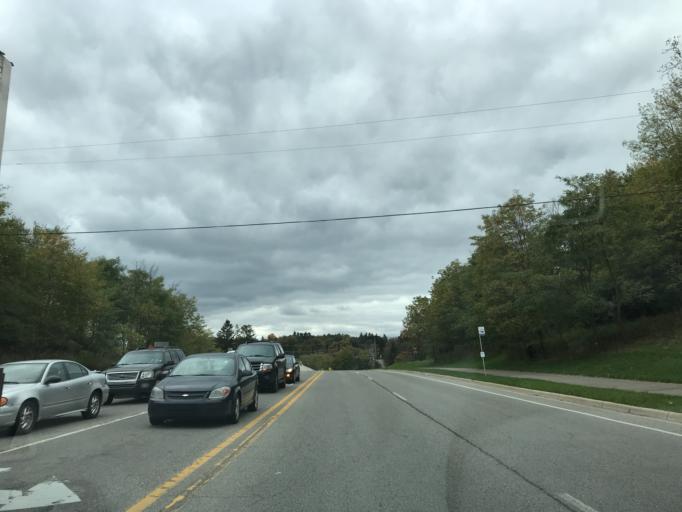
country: US
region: Michigan
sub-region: Washtenaw County
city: Ypsilanti
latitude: 42.2742
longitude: -83.6712
